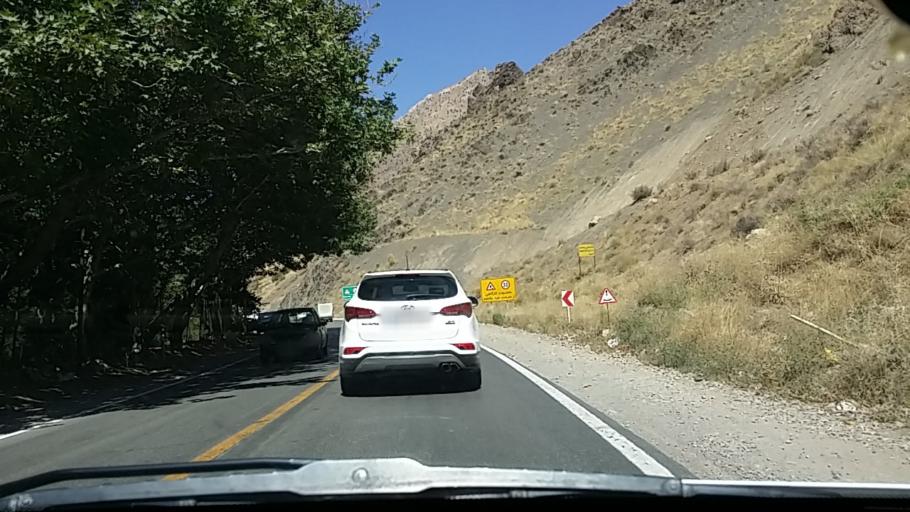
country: IR
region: Tehran
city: Tajrish
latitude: 36.0406
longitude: 51.3112
